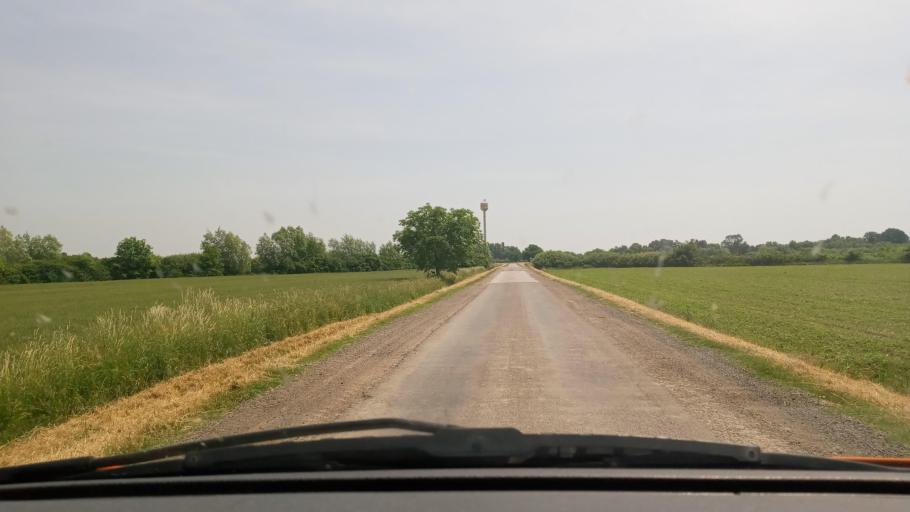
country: HU
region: Baranya
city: Szigetvar
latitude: 45.9807
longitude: 17.7395
